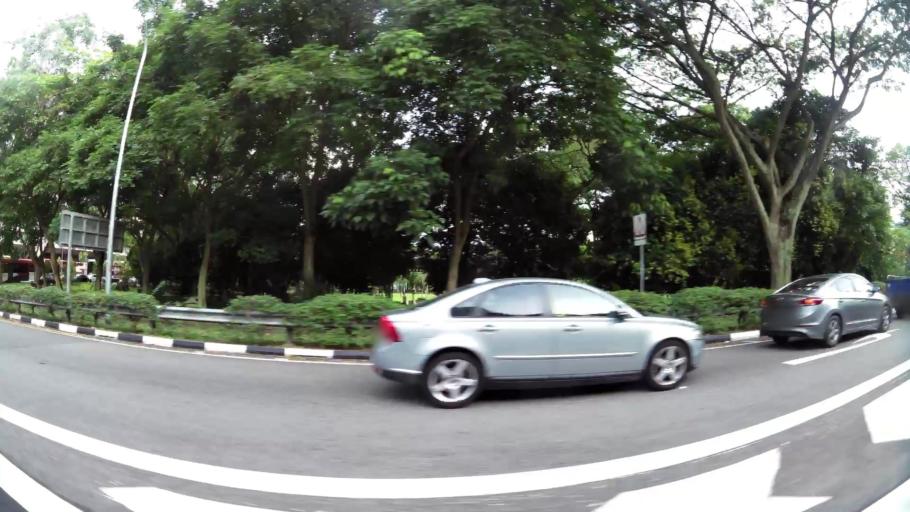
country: SG
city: Singapore
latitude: 1.3309
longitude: 103.8461
